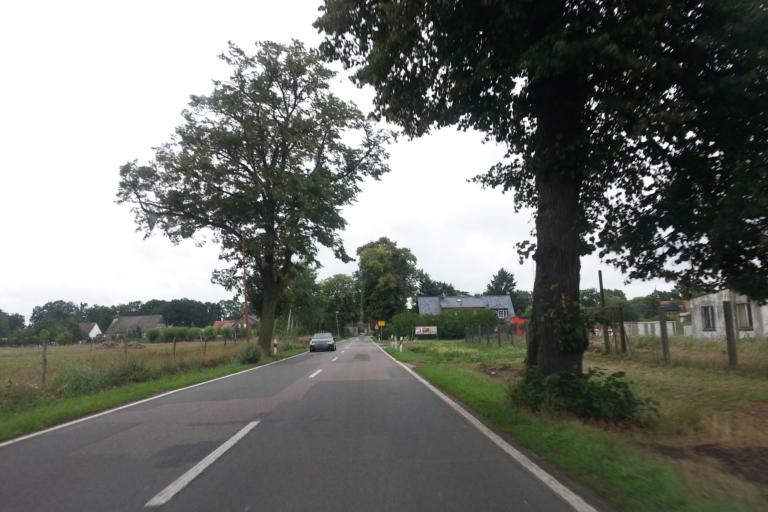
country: DE
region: Mecklenburg-Vorpommern
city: Ferdinandshof
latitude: 53.6796
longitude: 13.9159
